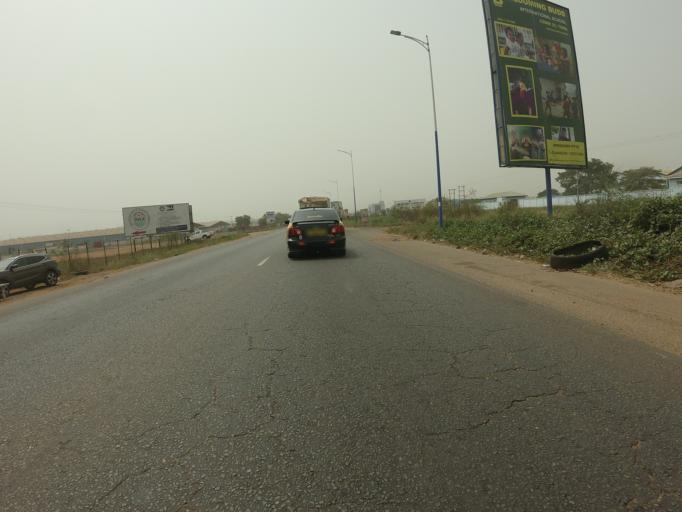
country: GH
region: Greater Accra
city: Tema
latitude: 5.7248
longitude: 0.0219
